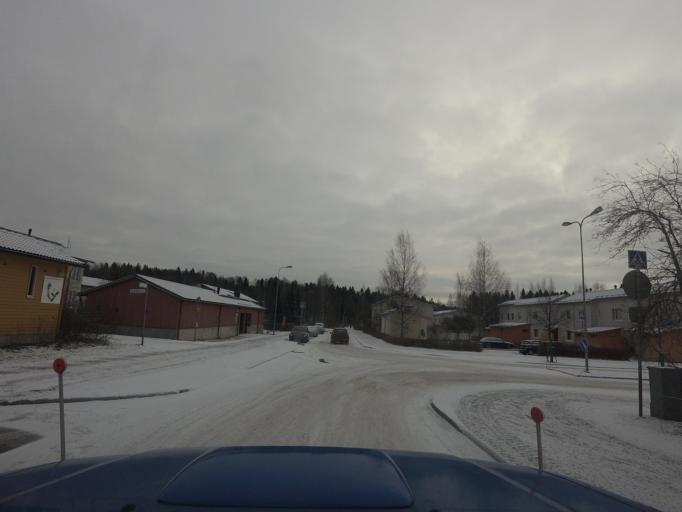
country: FI
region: Uusimaa
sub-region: Helsinki
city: Kilo
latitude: 60.2334
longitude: 24.7822
